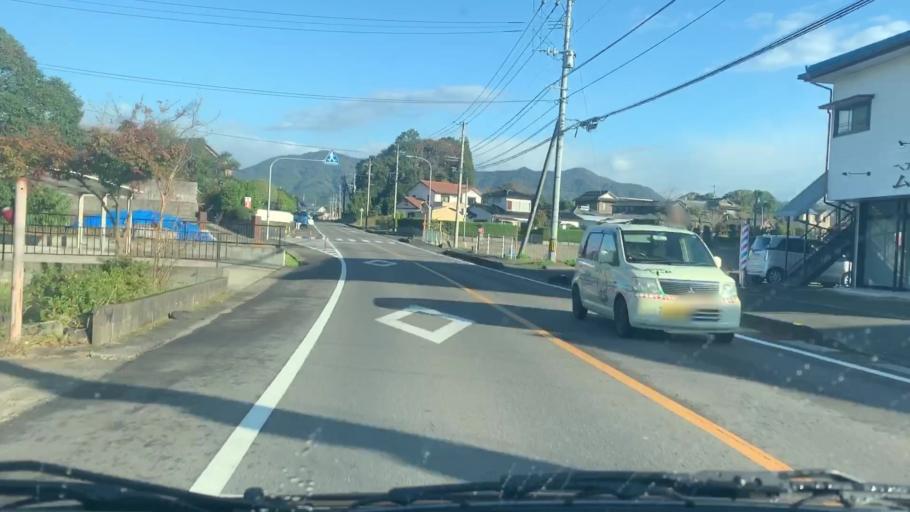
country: JP
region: Saga Prefecture
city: Takeocho-takeo
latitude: 33.2114
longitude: 130.0289
